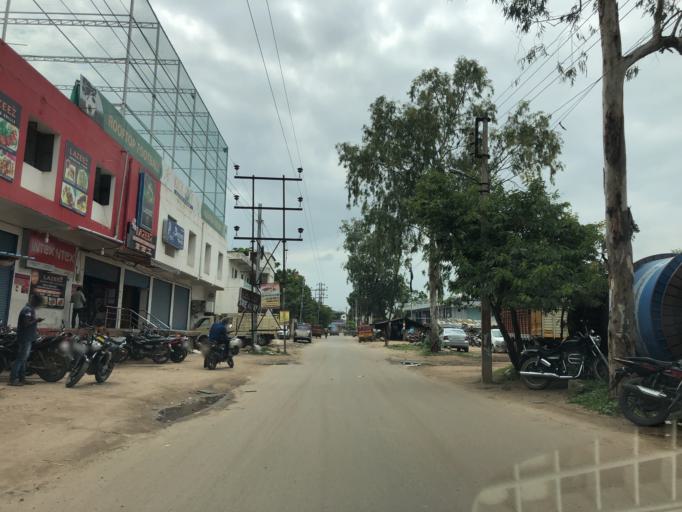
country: IN
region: Telangana
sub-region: Rangareddi
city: Quthbullapur
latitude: 17.4802
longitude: 78.4753
